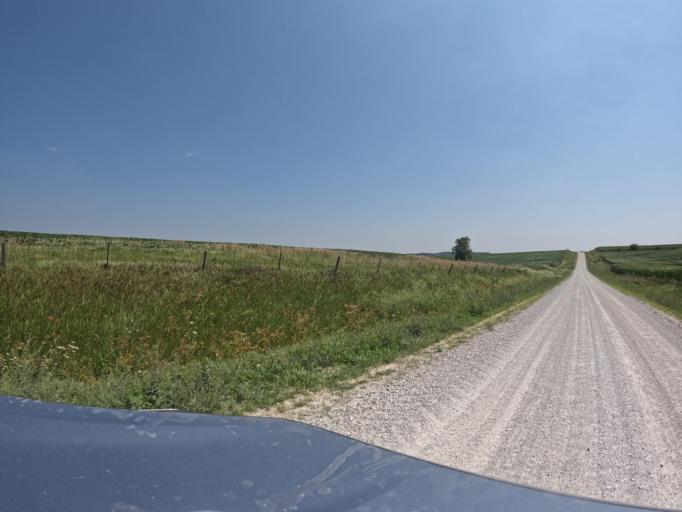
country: US
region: Iowa
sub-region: Keokuk County
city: Sigourney
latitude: 41.3323
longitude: -92.2385
